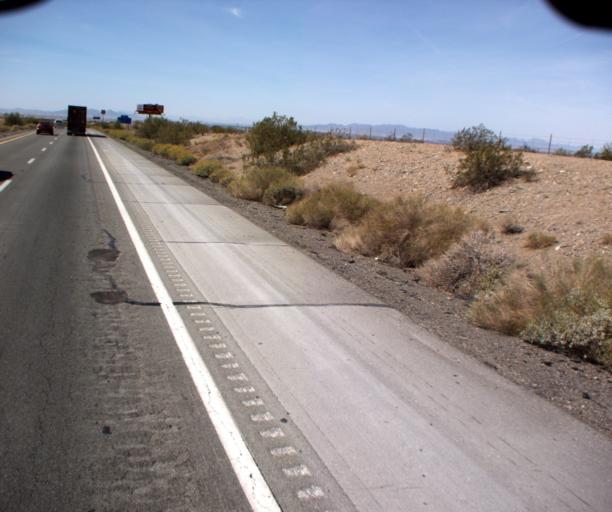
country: US
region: Arizona
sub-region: La Paz County
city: Ehrenberg
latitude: 33.6274
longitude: -114.4240
